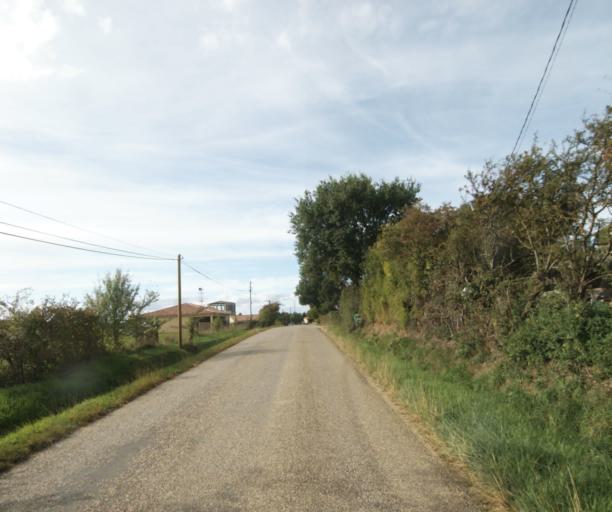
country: FR
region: Midi-Pyrenees
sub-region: Departement du Gers
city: Gondrin
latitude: 43.8770
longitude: 0.2355
